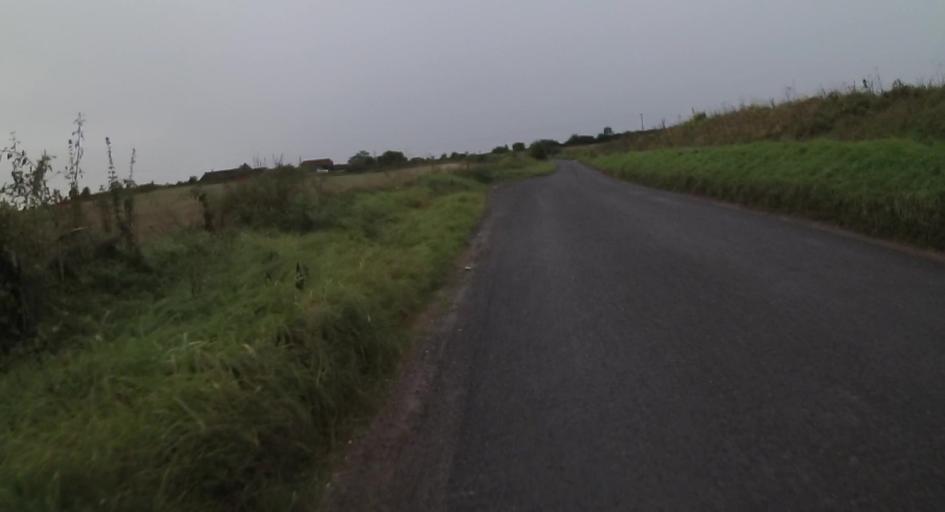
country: GB
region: England
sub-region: Hampshire
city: Basingstoke
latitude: 51.2889
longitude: -1.1372
